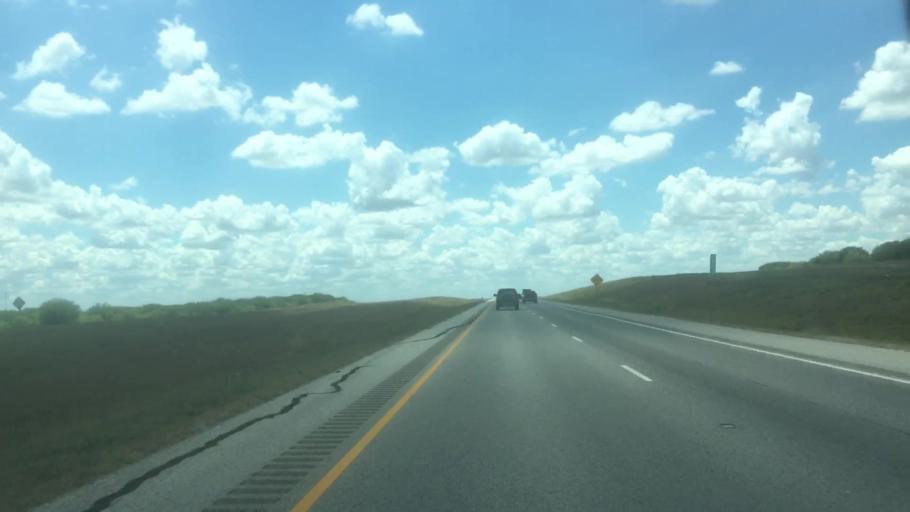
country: US
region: Texas
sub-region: Caldwell County
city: Martindale
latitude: 29.8089
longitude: -97.7700
